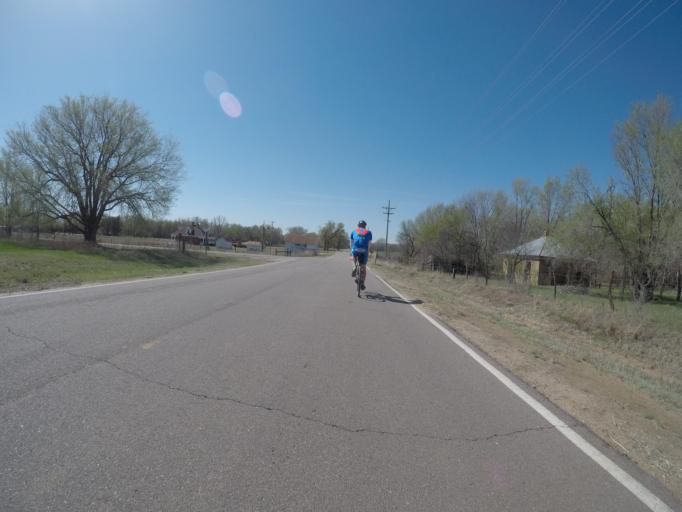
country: US
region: Kansas
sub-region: Pratt County
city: Pratt
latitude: 37.3805
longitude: -98.9209
